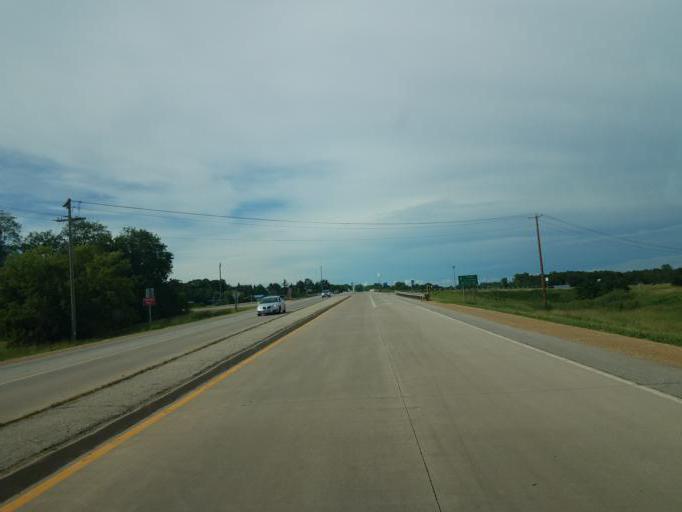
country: US
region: Wisconsin
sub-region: Monroe County
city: Tomah
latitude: 43.9551
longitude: -90.5047
